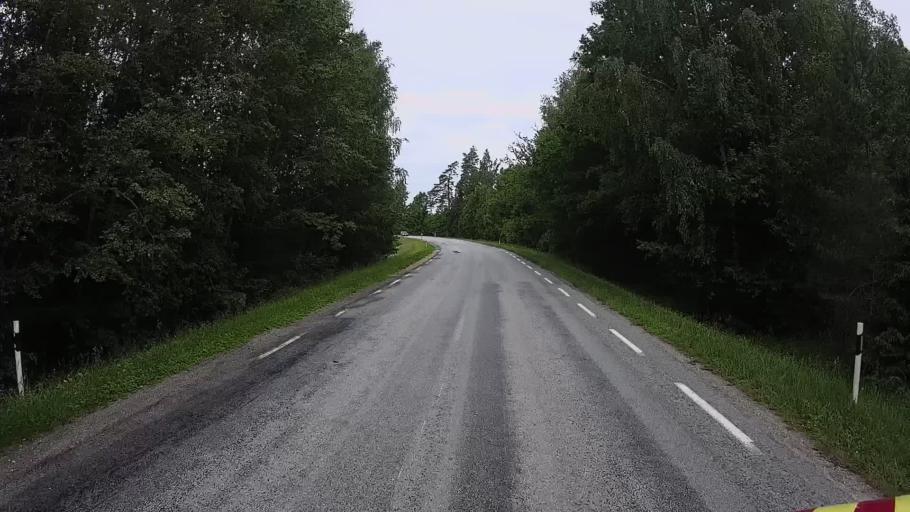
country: EE
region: Viljandimaa
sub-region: Karksi vald
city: Karksi-Nuia
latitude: 58.2229
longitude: 25.6151
